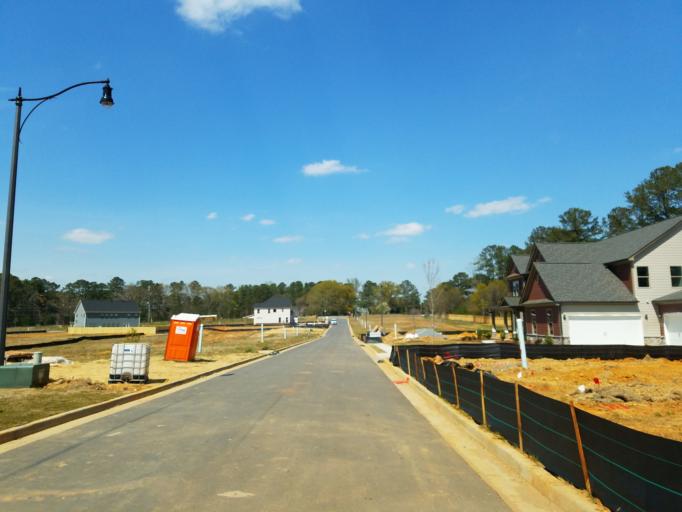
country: US
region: Georgia
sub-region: Cobb County
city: Powder Springs
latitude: 33.8994
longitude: -84.6211
